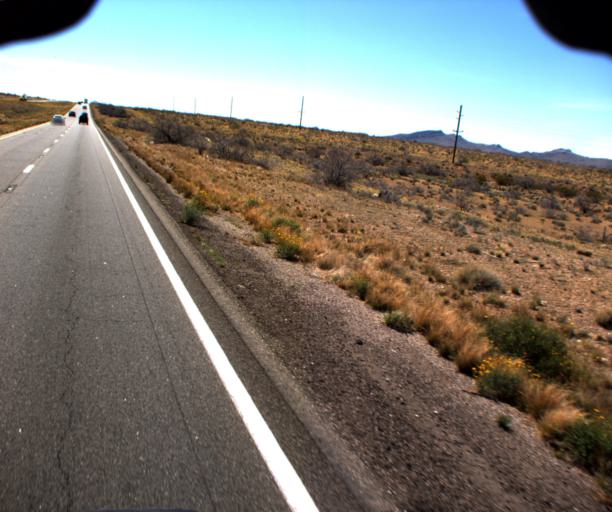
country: US
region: Arizona
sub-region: Mohave County
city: Dolan Springs
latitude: 35.4330
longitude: -114.2857
